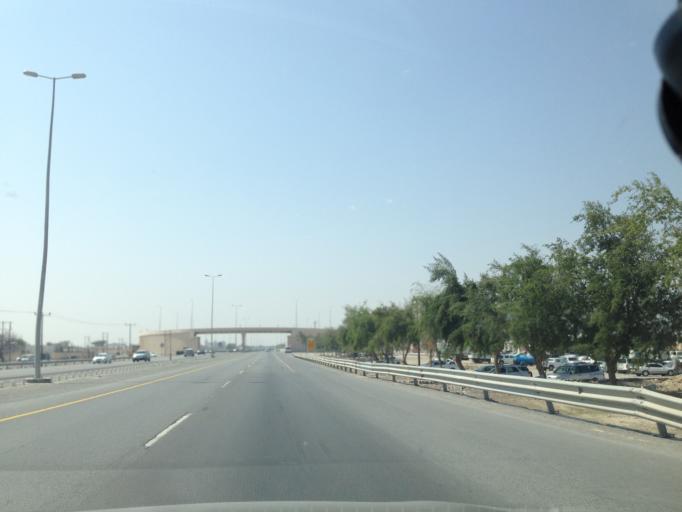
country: OM
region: Al Batinah
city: Barka'
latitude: 23.6639
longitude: 57.9507
